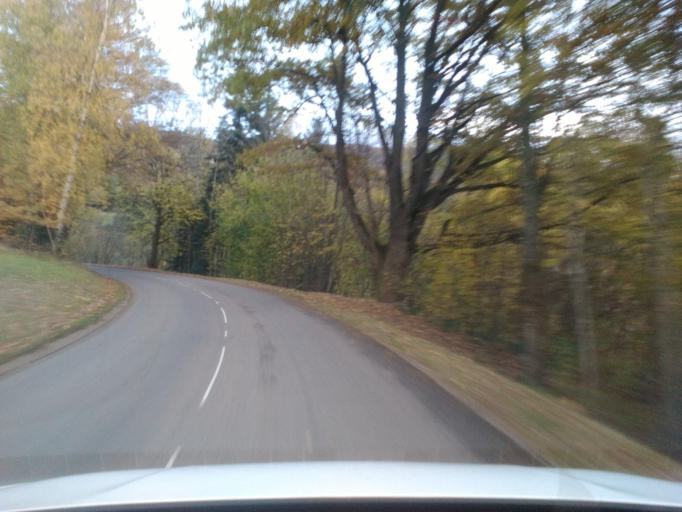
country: FR
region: Lorraine
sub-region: Departement des Vosges
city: Plainfaing
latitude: 48.1874
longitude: 7.0179
